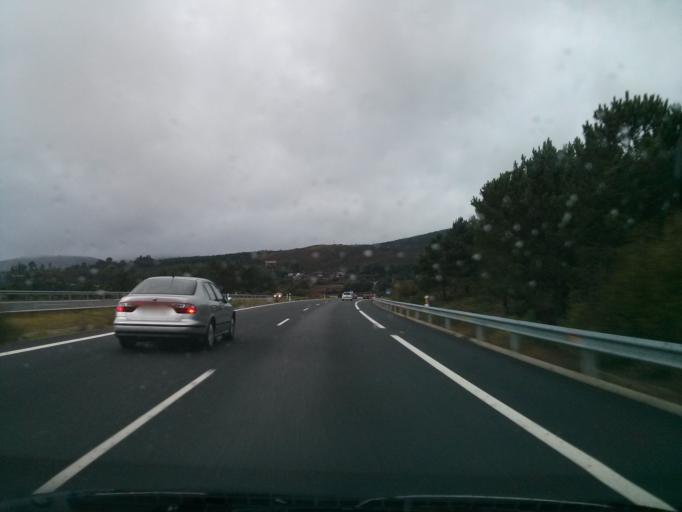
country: ES
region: Galicia
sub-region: Provincia de Pontevedra
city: Covelo
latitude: 42.1981
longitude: -8.3000
